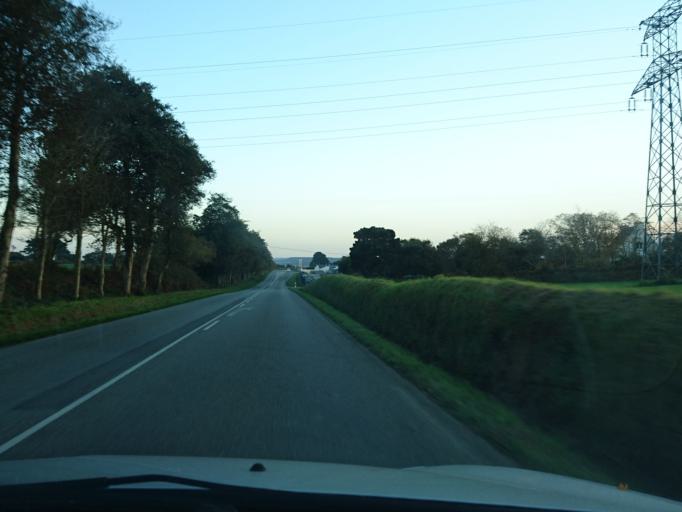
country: FR
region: Brittany
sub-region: Departement du Finistere
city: Saint-Renan
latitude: 48.4521
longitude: -4.6243
